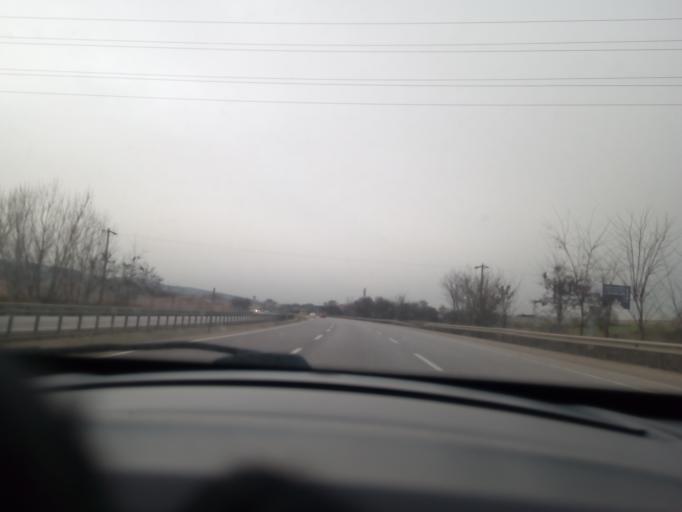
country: TR
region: Balikesir
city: Susurluk
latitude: 39.9640
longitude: 28.1703
